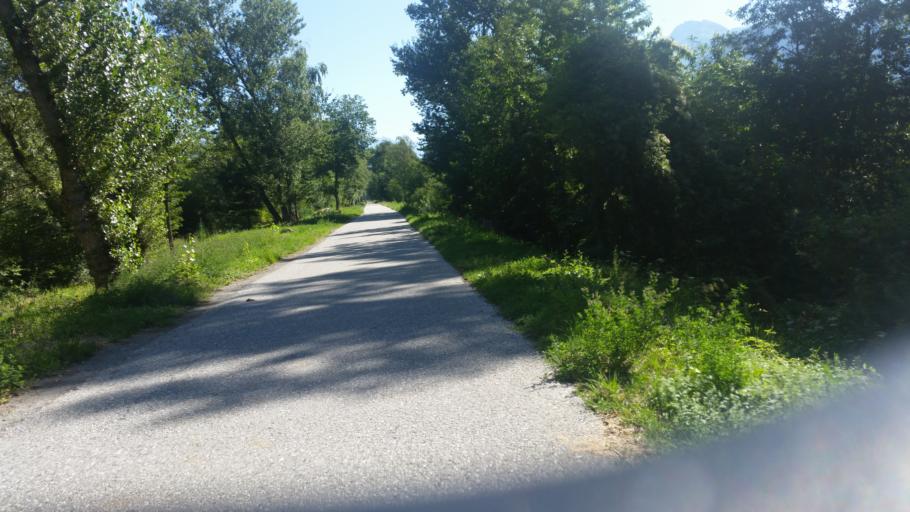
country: CH
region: Valais
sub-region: Sierre District
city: Grone
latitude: 46.2669
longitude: 7.4689
